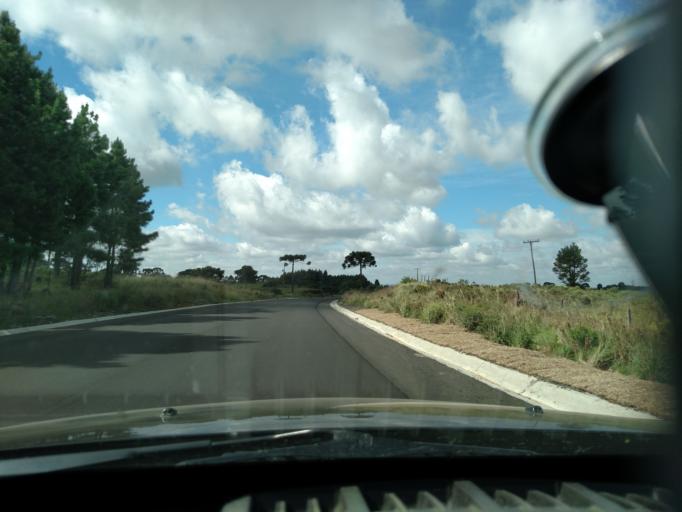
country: BR
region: Santa Catarina
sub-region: Sao Joaquim
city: Sao Joaquim
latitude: -28.0423
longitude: -50.0727
